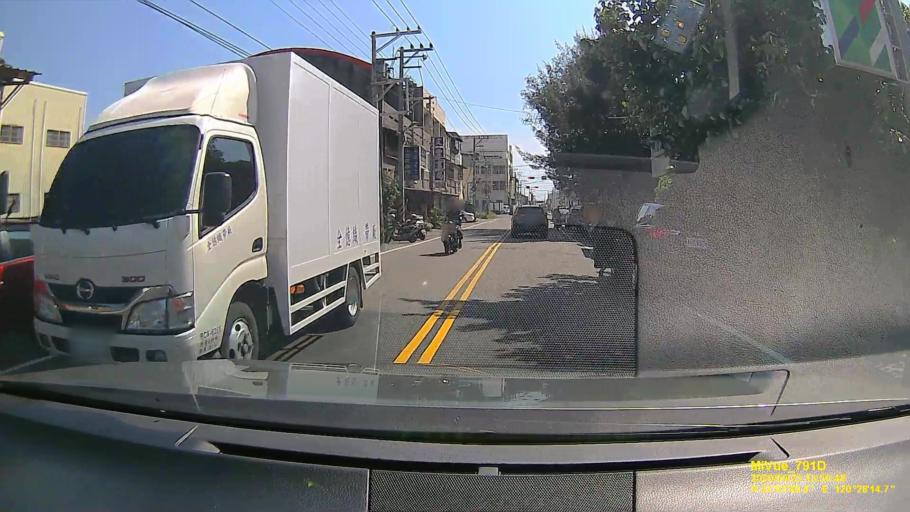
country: TW
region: Taiwan
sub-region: Changhua
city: Chang-hua
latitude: 24.1300
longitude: 120.4707
